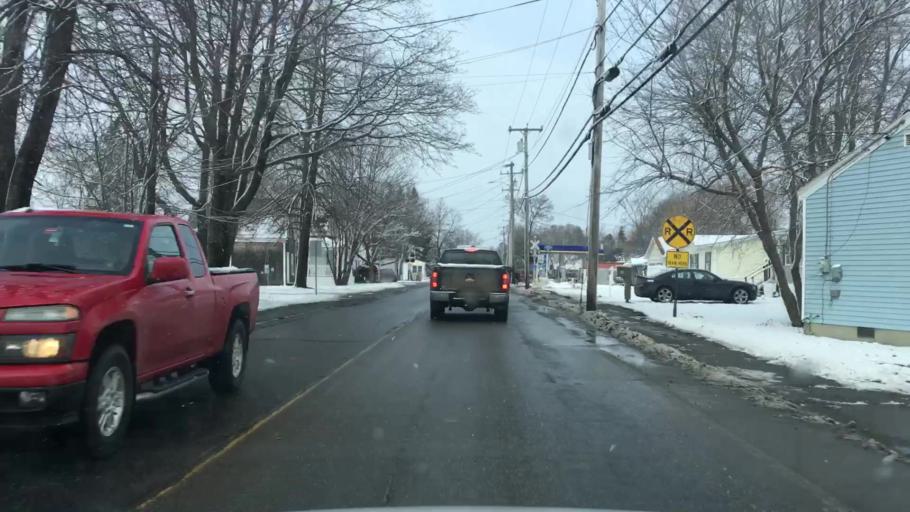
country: US
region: Maine
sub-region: Knox County
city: Rockland
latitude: 44.0946
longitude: -69.1107
